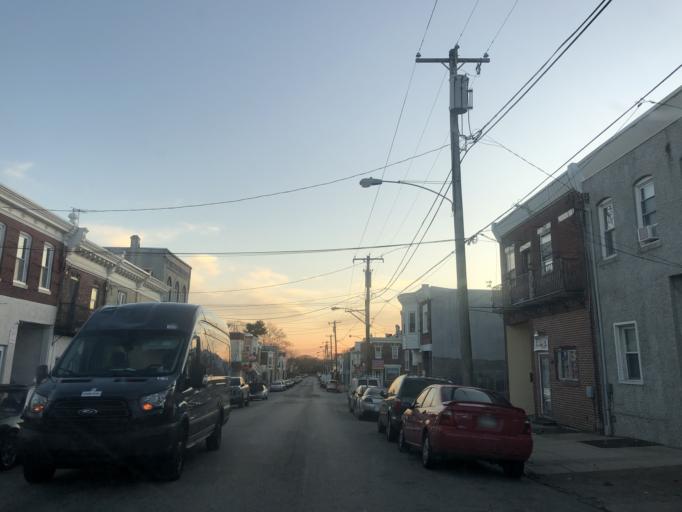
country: US
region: Pennsylvania
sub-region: Delaware County
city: Millbourne
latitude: 39.9697
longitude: -75.2474
